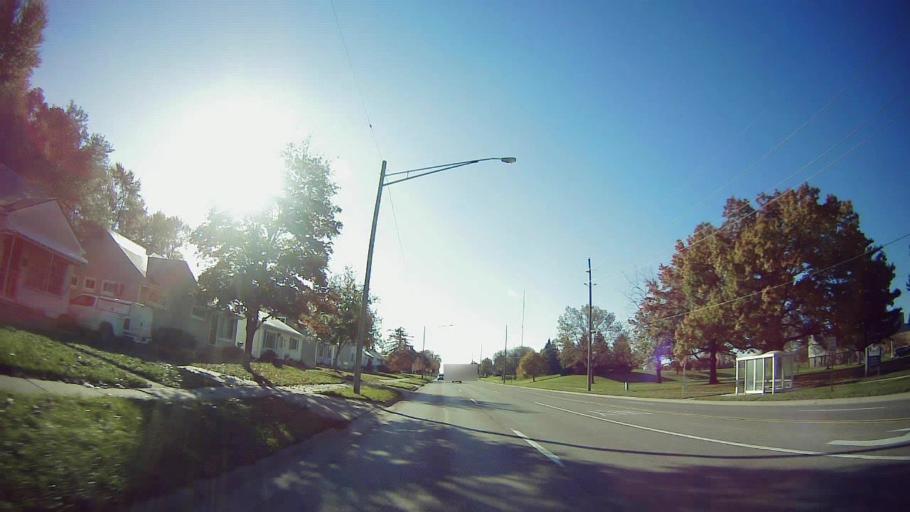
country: US
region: Michigan
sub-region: Oakland County
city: Lathrup Village
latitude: 42.4919
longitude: -83.2025
